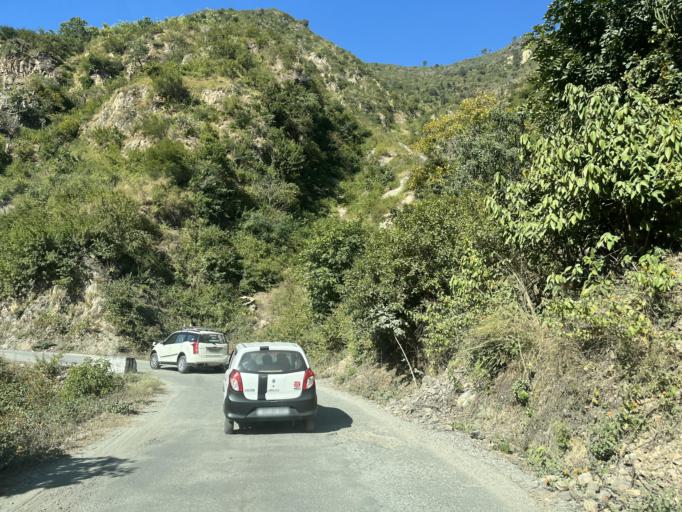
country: IN
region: Uttarakhand
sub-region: Naini Tal
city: Naini Tal
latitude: 29.5112
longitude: 79.4677
